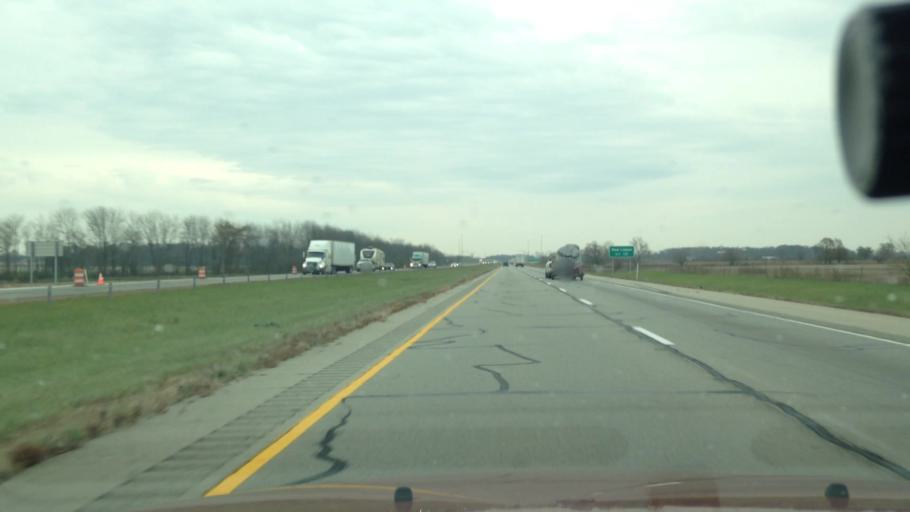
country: US
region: Indiana
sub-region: Wayne County
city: Cambridge City
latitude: 39.8520
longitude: -85.2794
